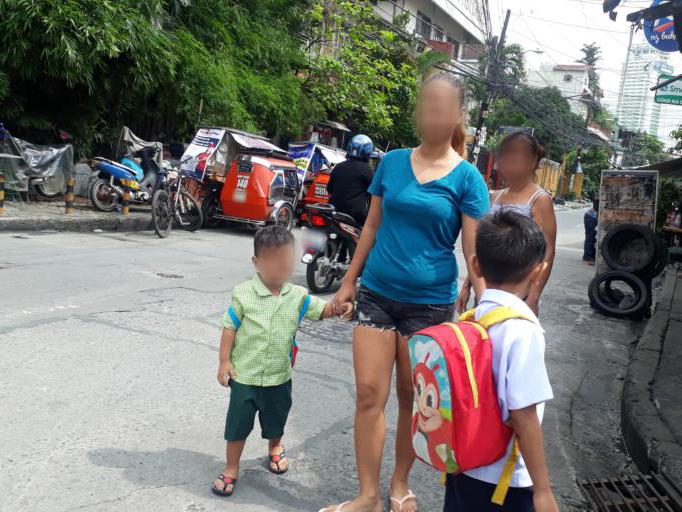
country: PH
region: Metro Manila
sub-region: San Juan
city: San Juan
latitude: 14.6159
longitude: 121.0477
